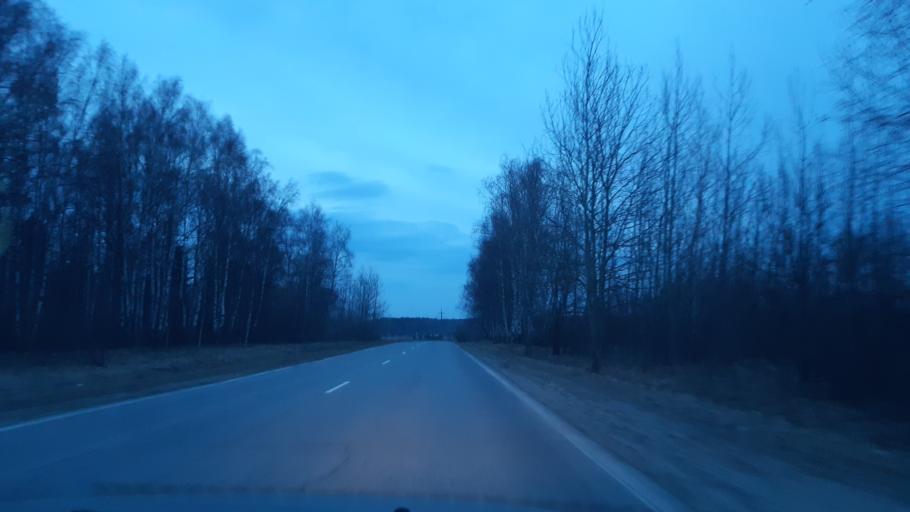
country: RU
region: Vladimir
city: Luknovo
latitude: 56.1924
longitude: 42.0284
